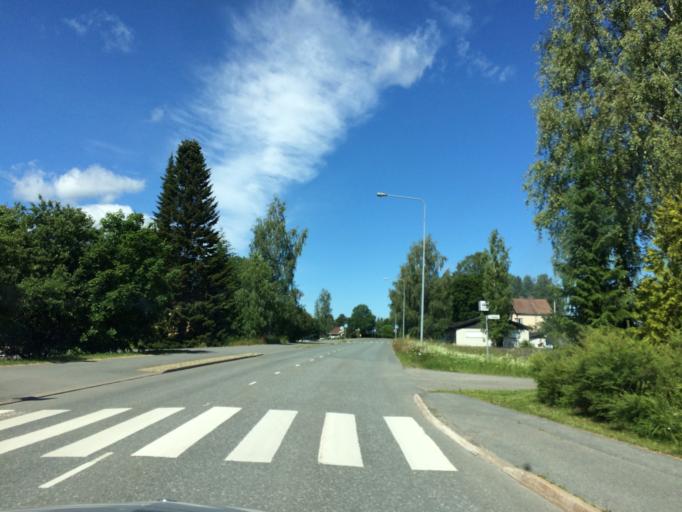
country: FI
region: Haeme
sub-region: Haemeenlinna
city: Haemeenlinna
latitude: 60.9649
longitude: 24.4748
